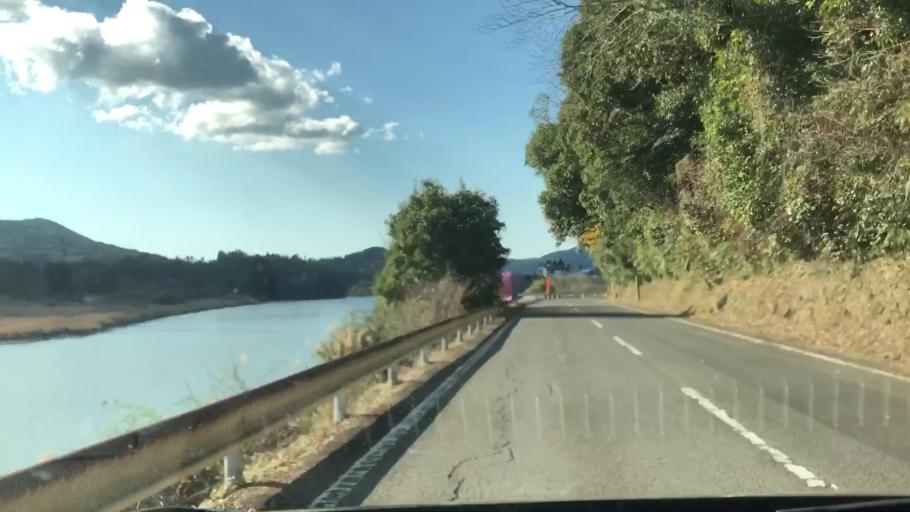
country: JP
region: Kagoshima
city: Satsumasendai
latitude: 31.8589
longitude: 130.3541
